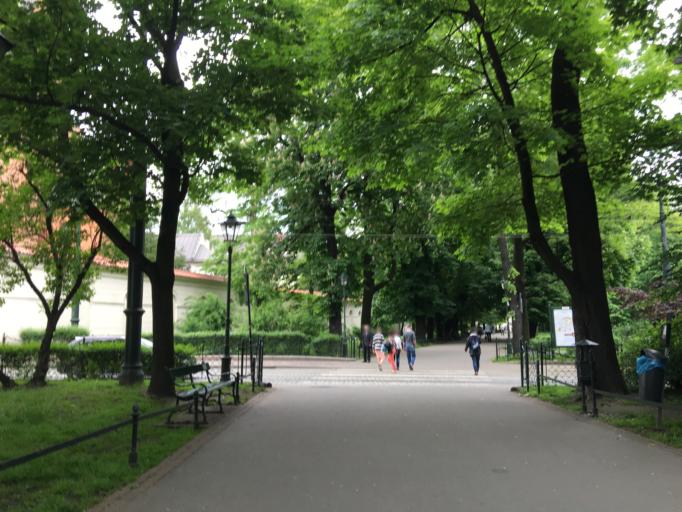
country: PL
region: Lesser Poland Voivodeship
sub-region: Krakow
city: Krakow
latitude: 50.0588
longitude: 19.9404
